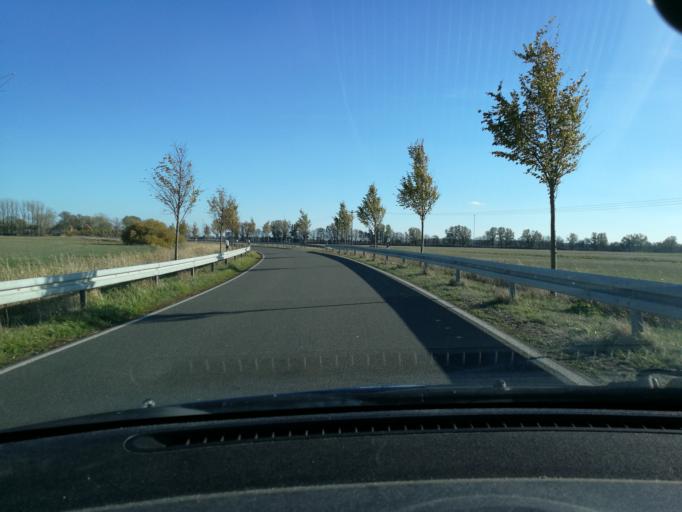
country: DE
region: Lower Saxony
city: Gorleben
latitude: 53.1092
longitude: 11.3696
